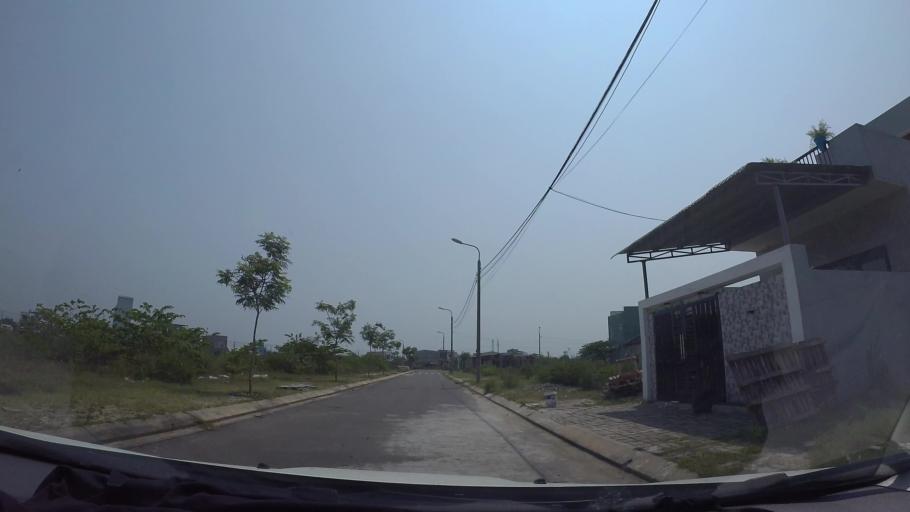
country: VN
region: Da Nang
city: Cam Le
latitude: 15.9915
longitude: 108.2017
